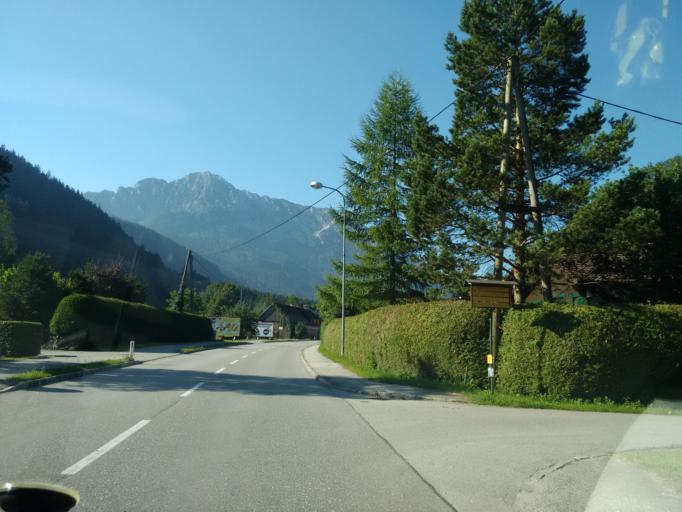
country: AT
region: Upper Austria
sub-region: Politischer Bezirk Kirchdorf an der Krems
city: Rossleithen
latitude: 47.6616
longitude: 14.3396
